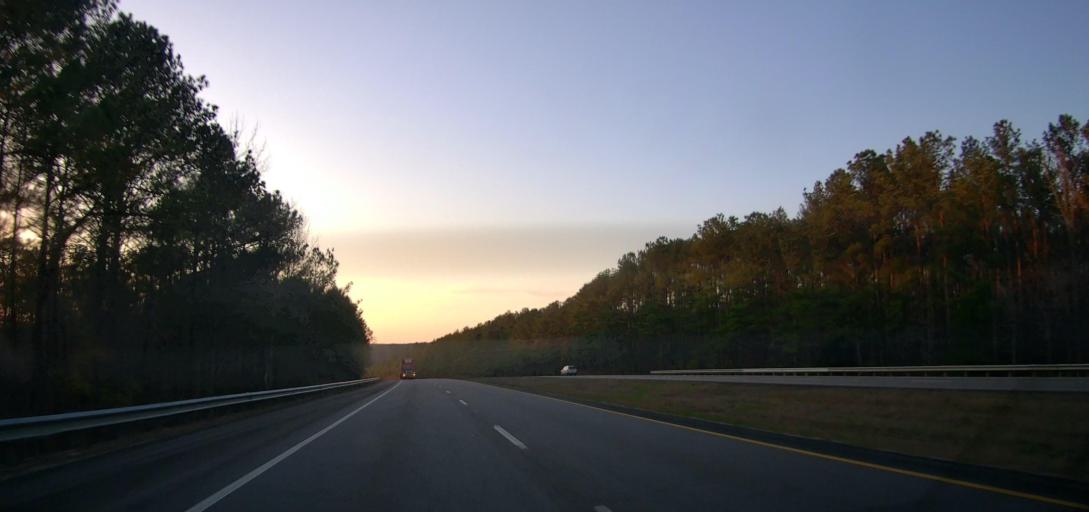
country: US
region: Alabama
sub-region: Coosa County
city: Goodwater
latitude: 33.0318
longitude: -86.1161
